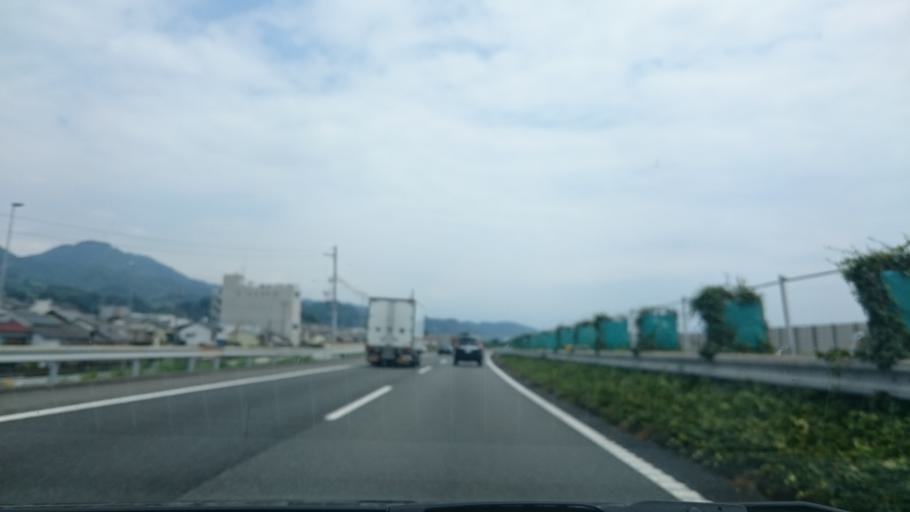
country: JP
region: Shizuoka
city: Fujinomiya
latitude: 35.1030
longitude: 138.5602
